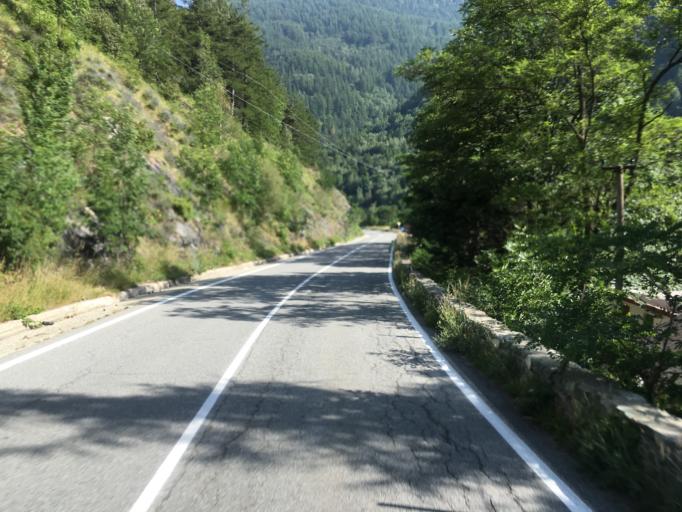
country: IT
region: Piedmont
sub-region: Provincia di Torino
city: Fenestrelle
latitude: 45.0288
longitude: 7.0564
